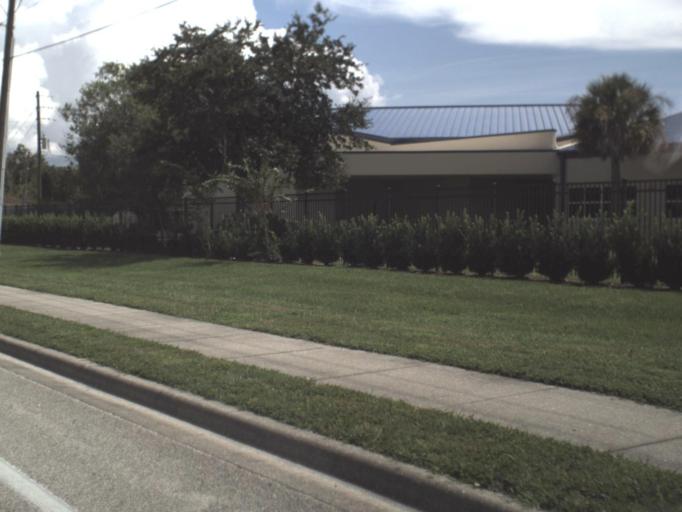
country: US
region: Florida
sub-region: Manatee County
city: Samoset
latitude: 27.4474
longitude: -82.5350
